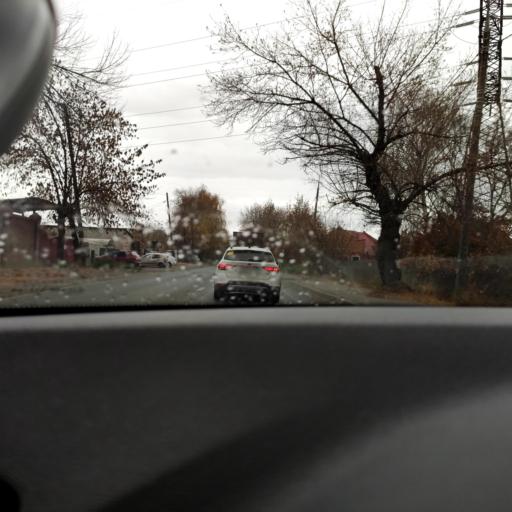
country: RU
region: Samara
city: Smyshlyayevka
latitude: 53.2364
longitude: 50.3177
